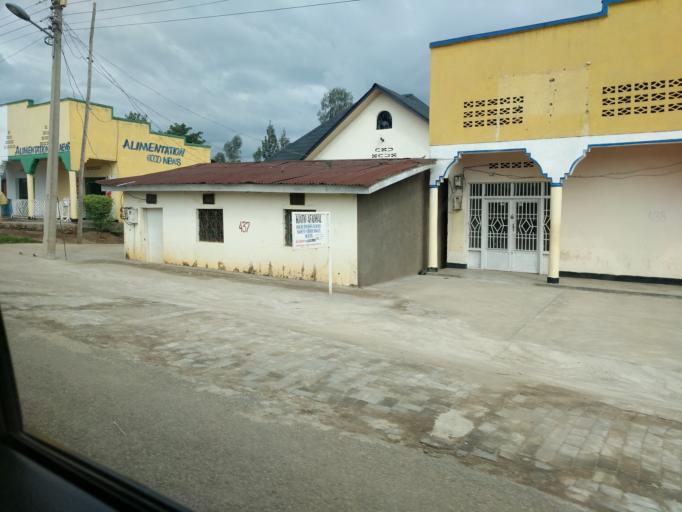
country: RW
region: Northern Province
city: Musanze
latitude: -1.5048
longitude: 29.6104
